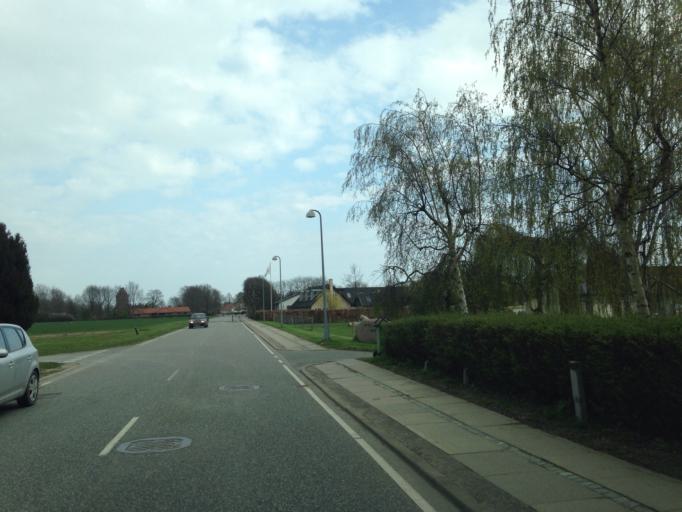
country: DK
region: Capital Region
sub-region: Hoje-Taastrup Kommune
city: Taastrup
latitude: 55.6276
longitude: 12.2925
